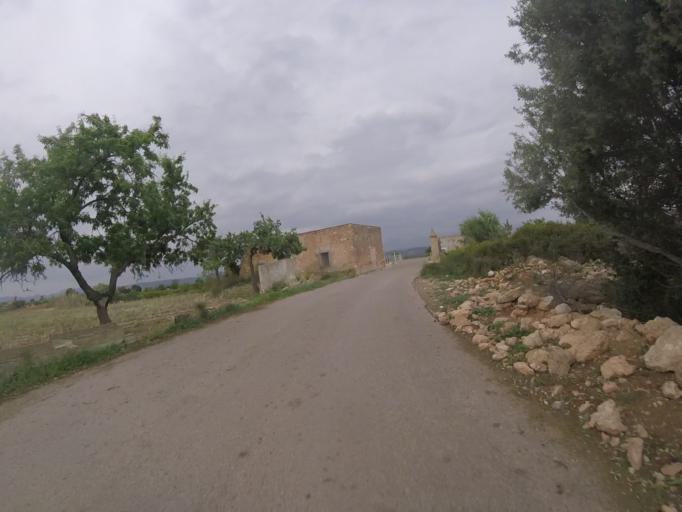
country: ES
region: Valencia
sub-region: Provincia de Castello
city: Torreblanca
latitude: 40.2141
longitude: 0.2393
